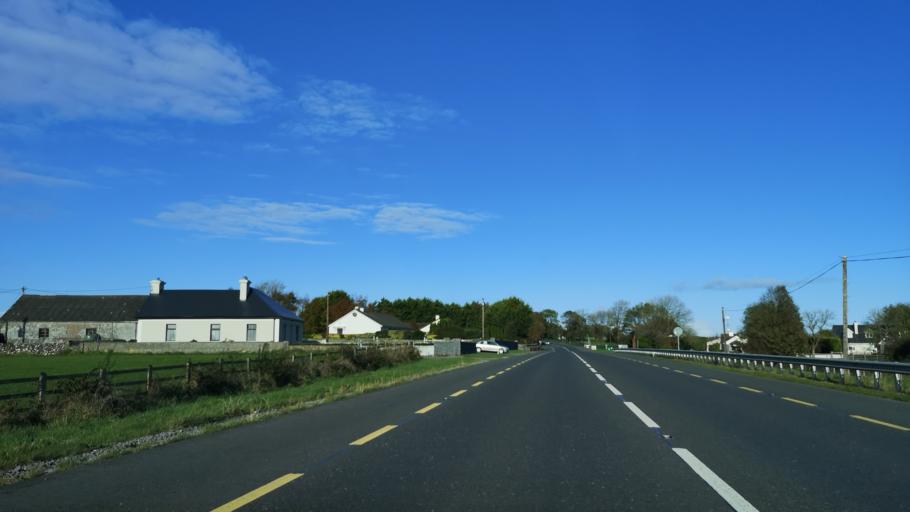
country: IE
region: Connaught
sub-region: County Galway
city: Moycullen
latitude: 53.4441
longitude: -9.0830
